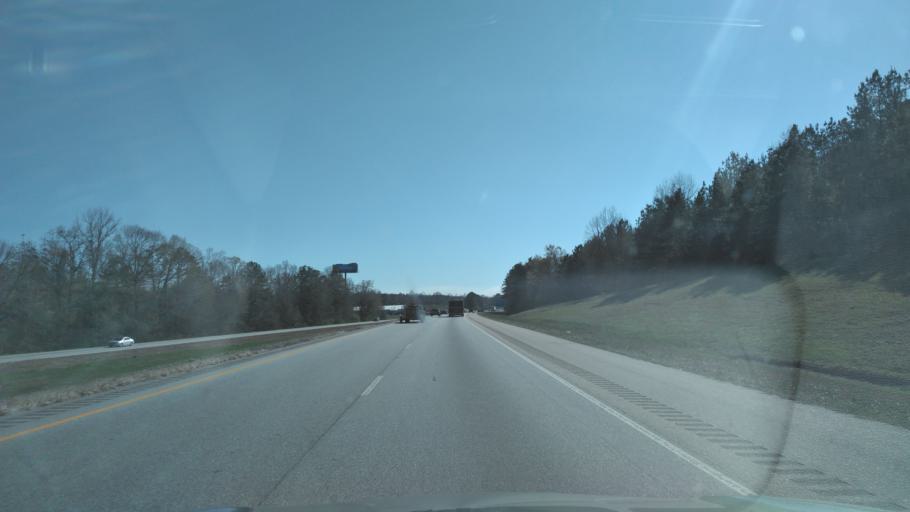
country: US
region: Alabama
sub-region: Lowndes County
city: Fort Deposit
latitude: 31.9942
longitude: -86.5260
